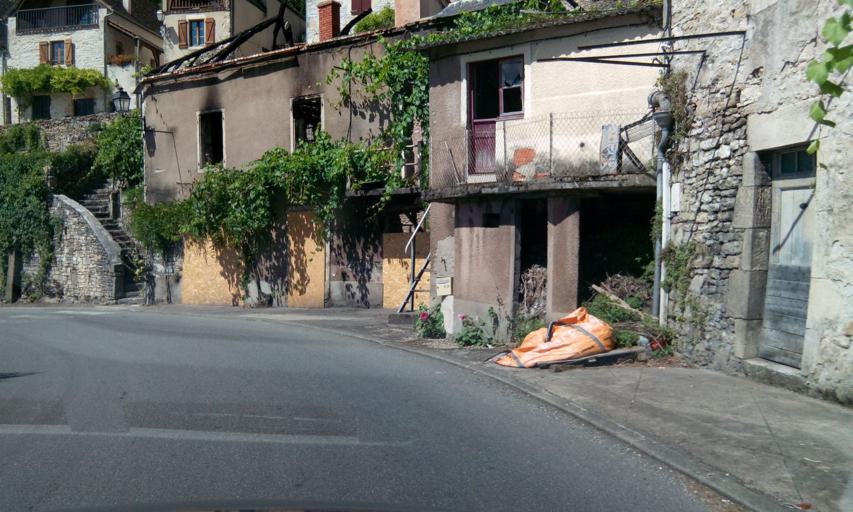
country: FR
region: Midi-Pyrenees
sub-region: Departement du Lot
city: Vayrac
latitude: 44.8807
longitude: 1.6199
